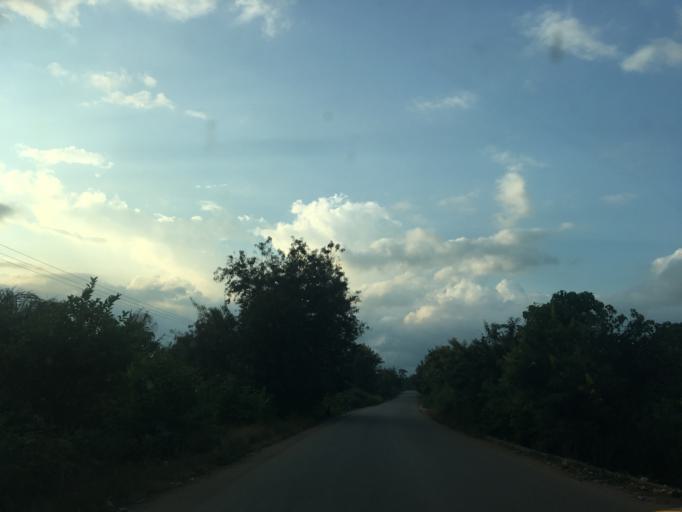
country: GH
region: Western
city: Bibiani
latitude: 6.6527
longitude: -2.4258
